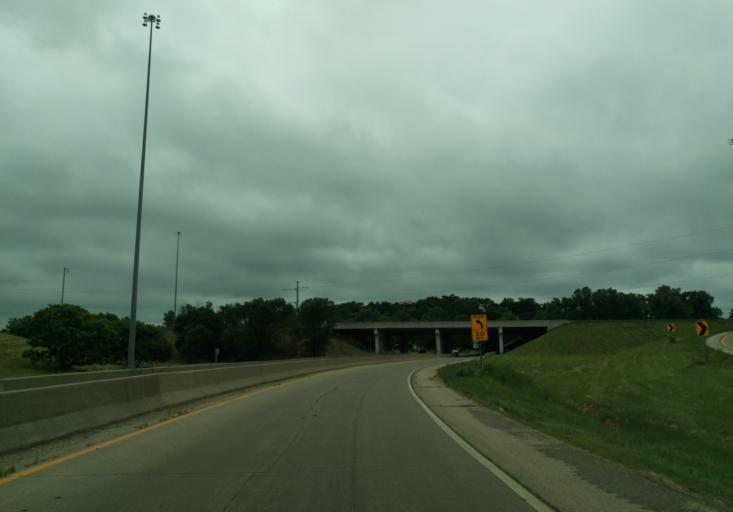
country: US
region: Wisconsin
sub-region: Dane County
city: Monona
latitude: 43.0444
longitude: -89.3707
